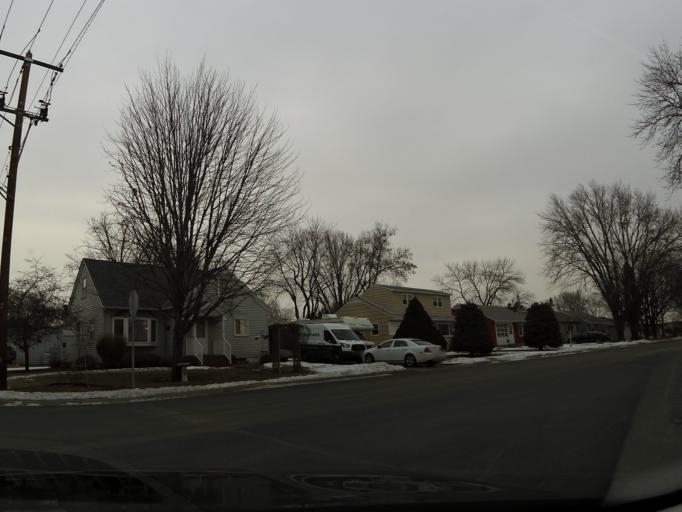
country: US
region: Minnesota
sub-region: Carver County
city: Waconia
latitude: 44.8481
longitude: -93.7785
